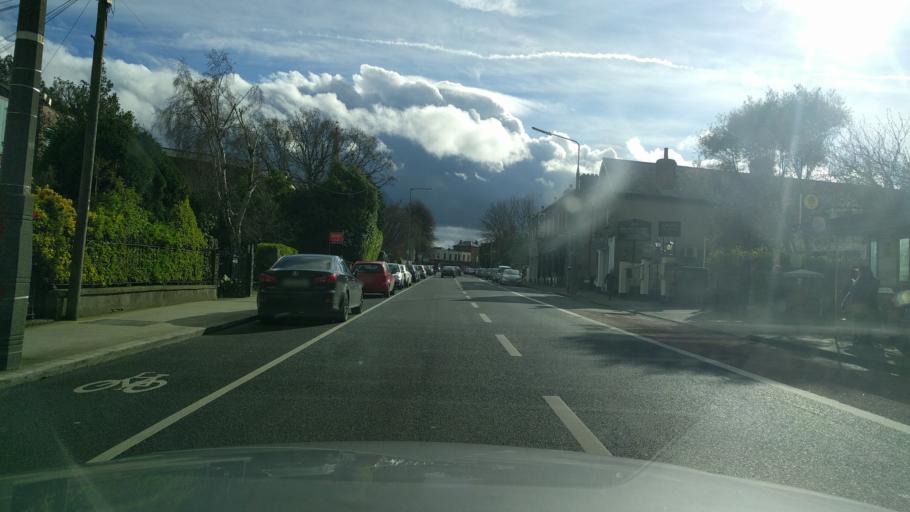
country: IE
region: Leinster
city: Rathgar
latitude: 53.3141
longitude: -6.2724
